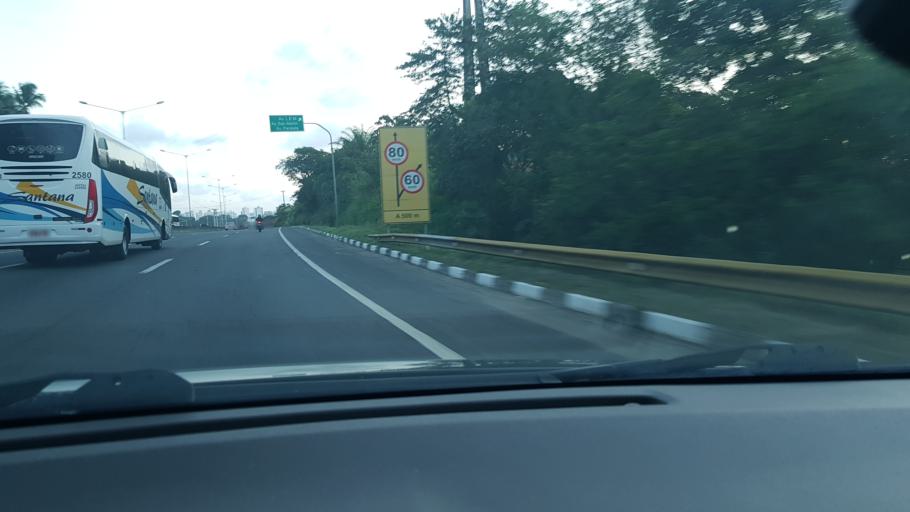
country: BR
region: Bahia
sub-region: Salvador
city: Salvador
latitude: -12.9487
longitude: -38.4700
